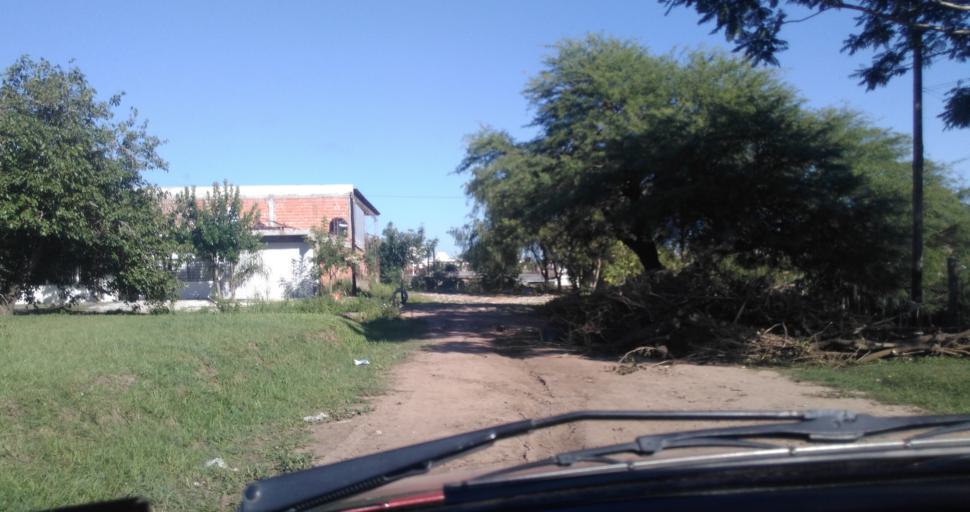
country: AR
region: Chaco
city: Resistencia
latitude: -27.4403
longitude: -58.9618
